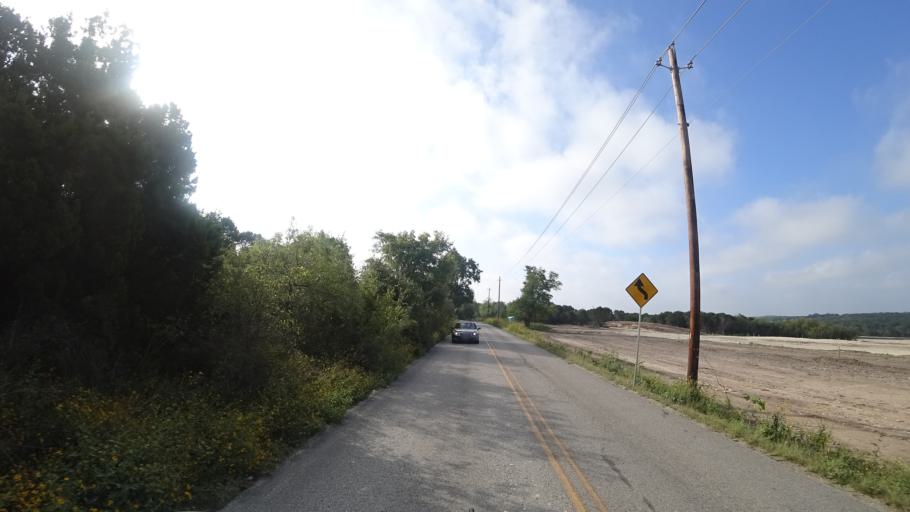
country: US
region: Texas
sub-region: Travis County
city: Pflugerville
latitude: 30.3577
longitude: -97.6488
